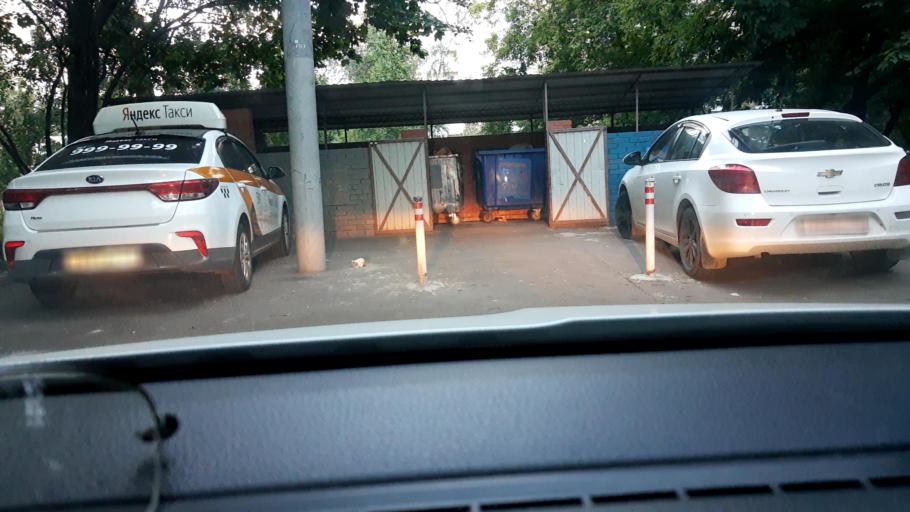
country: RU
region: Moscow
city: Davydkovo
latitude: 55.7201
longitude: 37.4551
